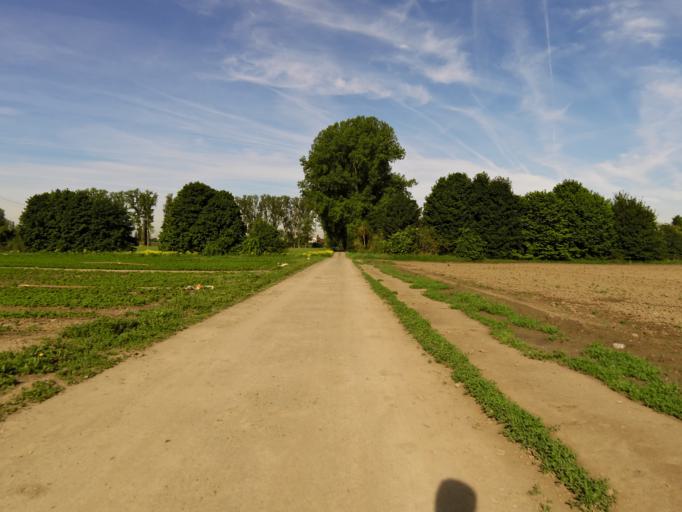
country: DE
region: Hesse
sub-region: Regierungsbezirk Darmstadt
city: Burstadt
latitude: 49.6275
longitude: 8.4723
